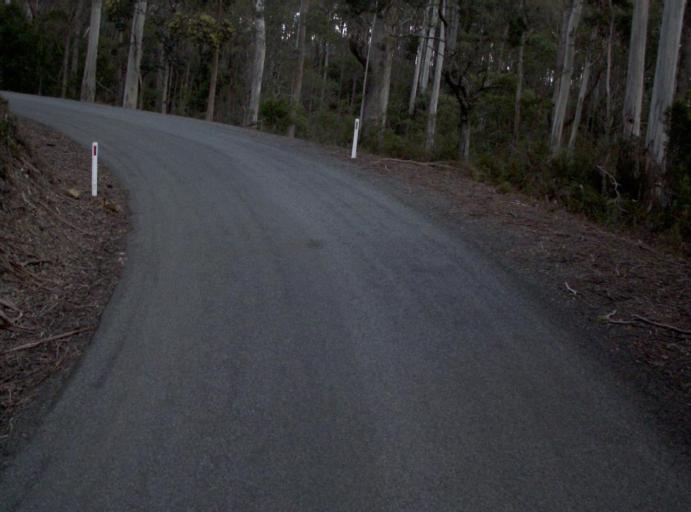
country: AU
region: Tasmania
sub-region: Launceston
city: Newstead
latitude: -41.3123
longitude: 147.3331
